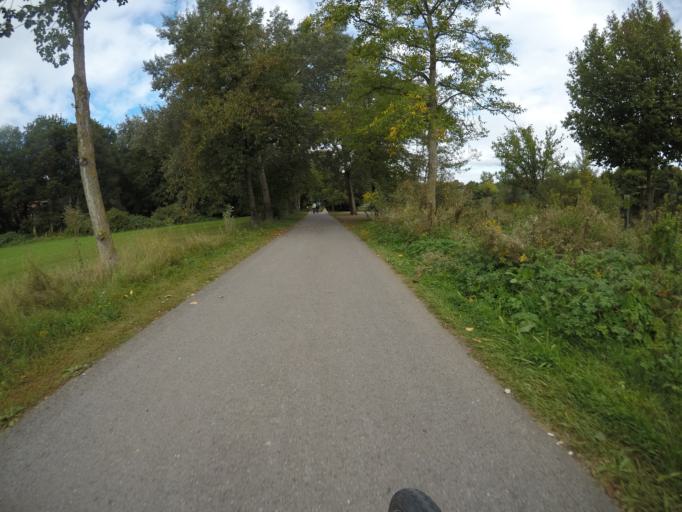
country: DE
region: Baden-Wuerttemberg
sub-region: Regierungsbezirk Stuttgart
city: Freiberg am Neckar
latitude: 48.9102
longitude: 9.2171
